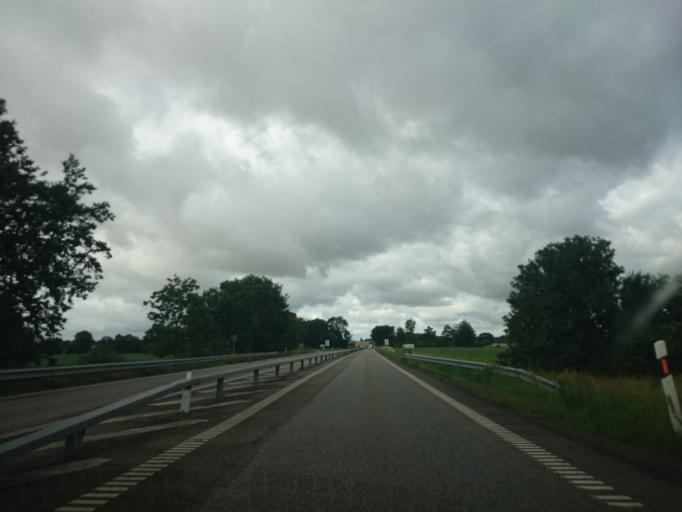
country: SE
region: Skane
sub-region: Hoors Kommun
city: Satofta
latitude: 55.8387
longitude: 13.5710
